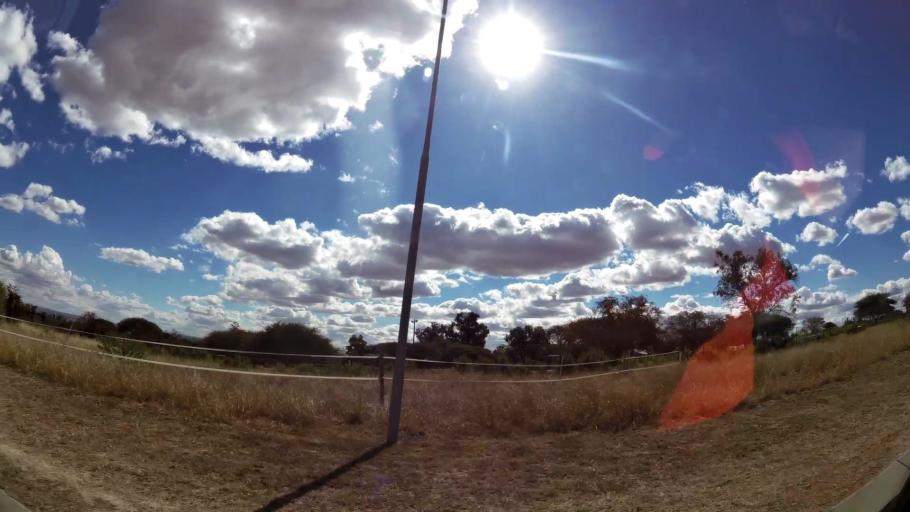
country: ZA
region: Limpopo
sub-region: Capricorn District Municipality
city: Polokwane
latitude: -23.8707
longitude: 29.4954
